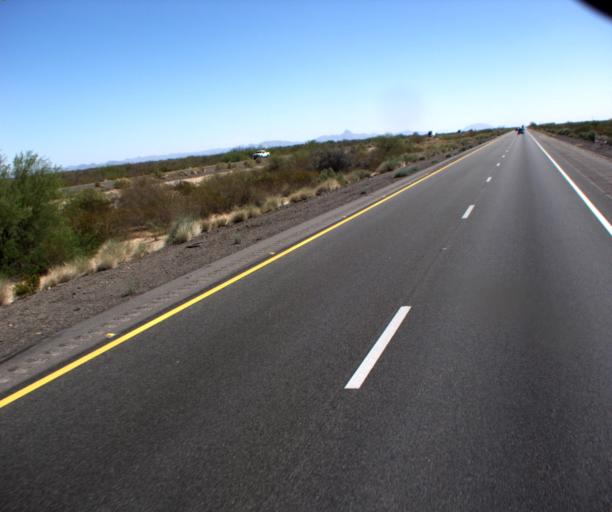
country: US
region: Arizona
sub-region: La Paz County
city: Salome
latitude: 33.5852
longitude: -113.4621
